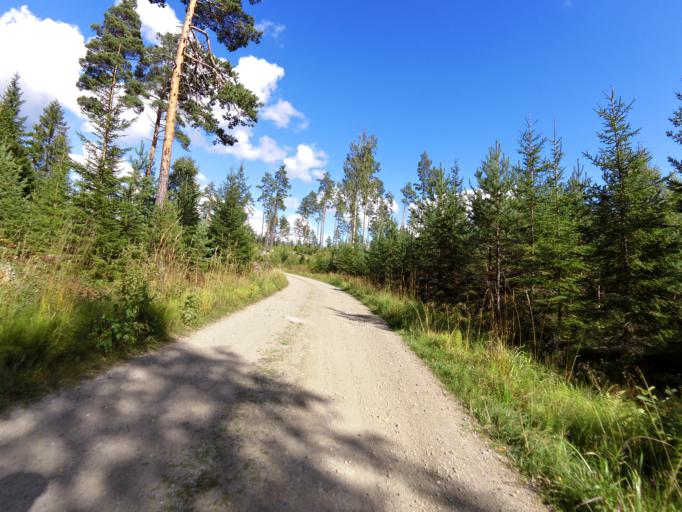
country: SE
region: Gaevleborg
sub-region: Ockelbo Kommun
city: Ockelbo
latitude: 60.8367
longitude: 16.8027
